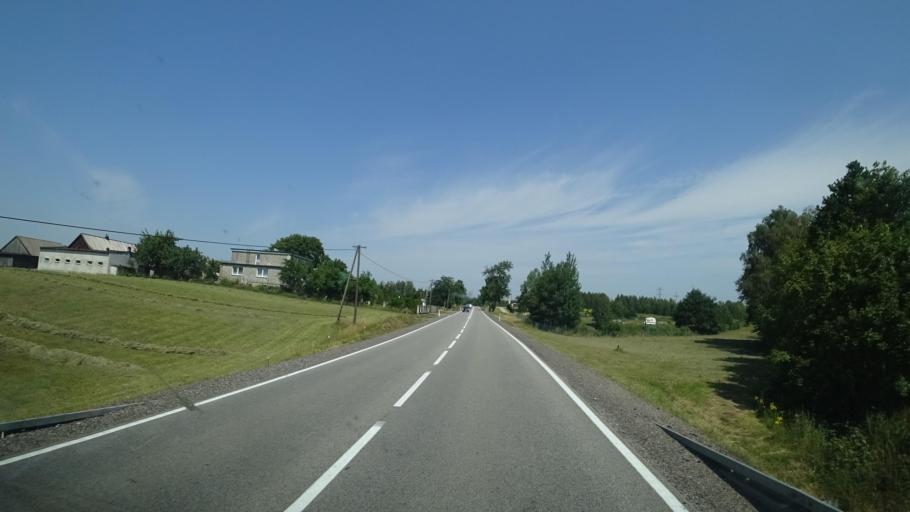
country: PL
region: Pomeranian Voivodeship
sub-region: Powiat koscierski
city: Koscierzyna
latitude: 54.1485
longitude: 18.0277
